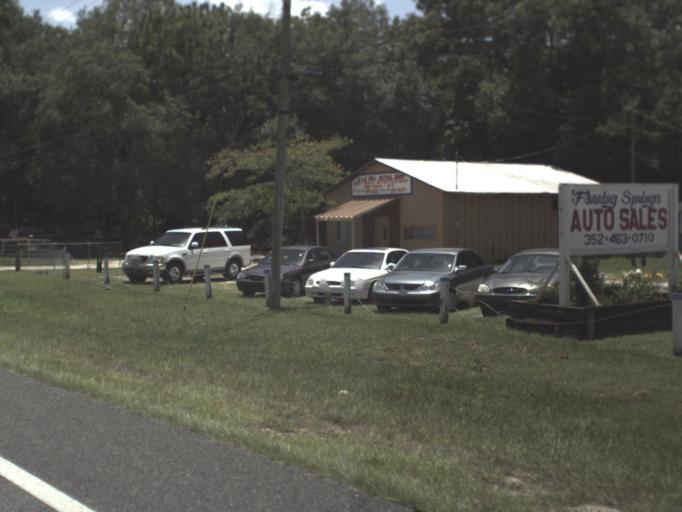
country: US
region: Florida
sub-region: Levy County
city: Manatee Road
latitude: 29.5727
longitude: -82.9139
